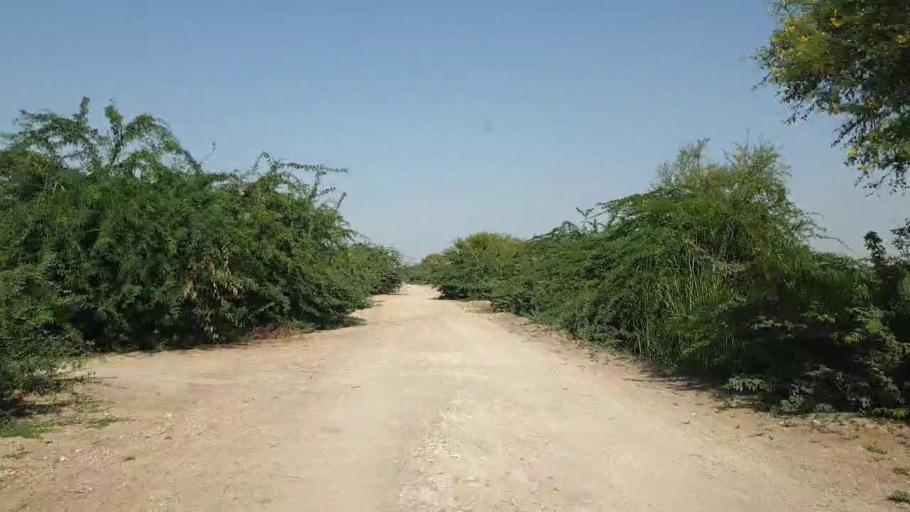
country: PK
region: Sindh
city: Tando Bago
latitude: 24.7508
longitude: 69.0284
